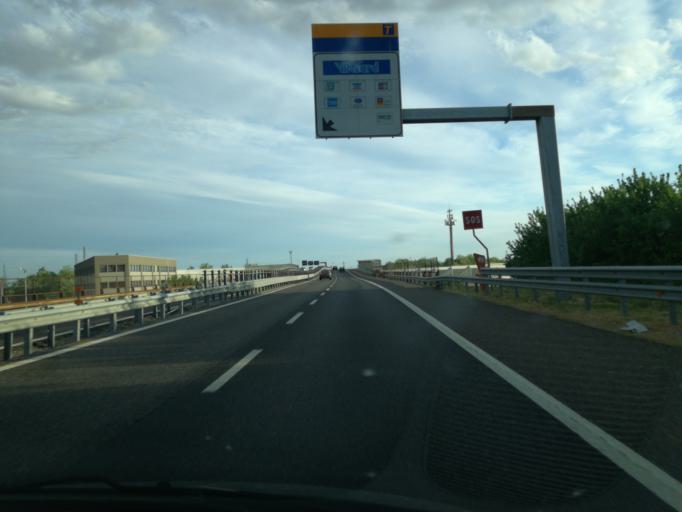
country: IT
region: Lombardy
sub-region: Provincia di Monza e Brianza
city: Agrate Brianza
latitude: 45.5683
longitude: 9.3370
